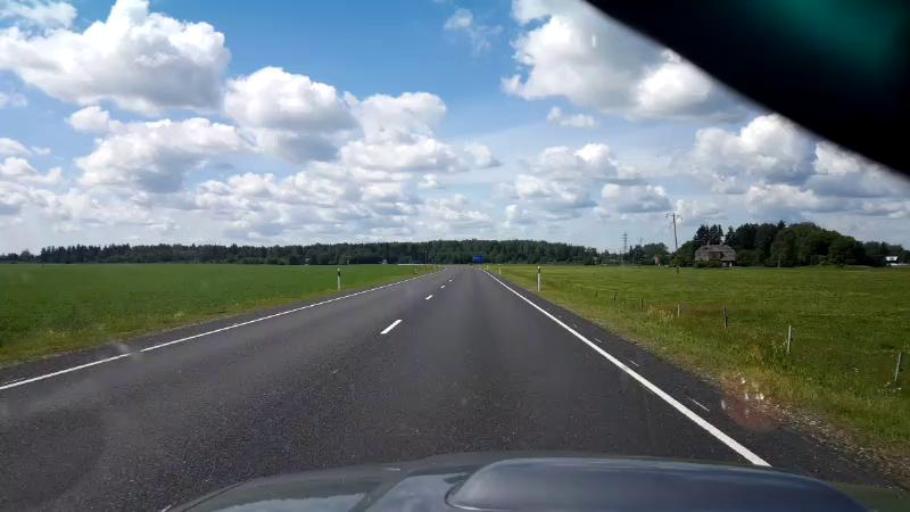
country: EE
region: Jaervamaa
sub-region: Jaerva-Jaani vald
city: Jarva-Jaani
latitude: 59.1384
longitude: 25.7663
